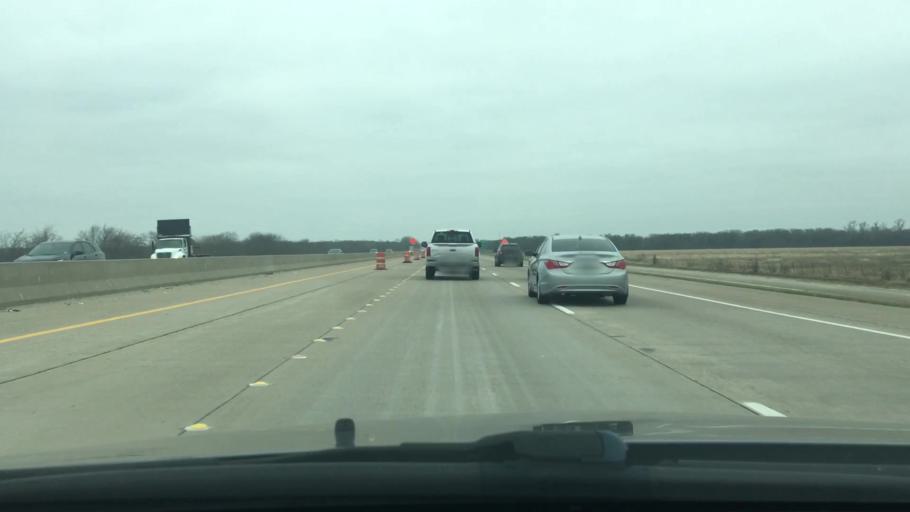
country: US
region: Texas
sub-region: Navarro County
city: Corsicana
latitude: 32.1729
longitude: -96.4706
